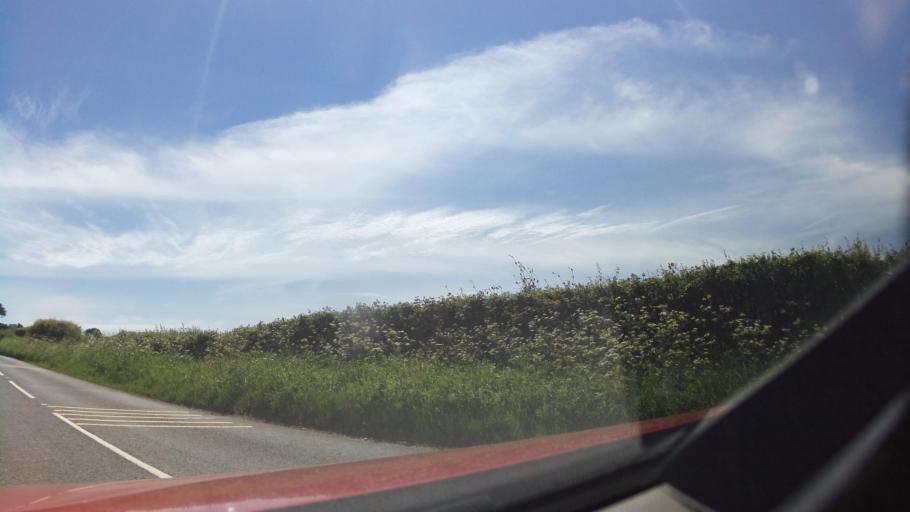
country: GB
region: England
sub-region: Devon
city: Ottery St Mary
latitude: 50.8238
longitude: -3.2854
